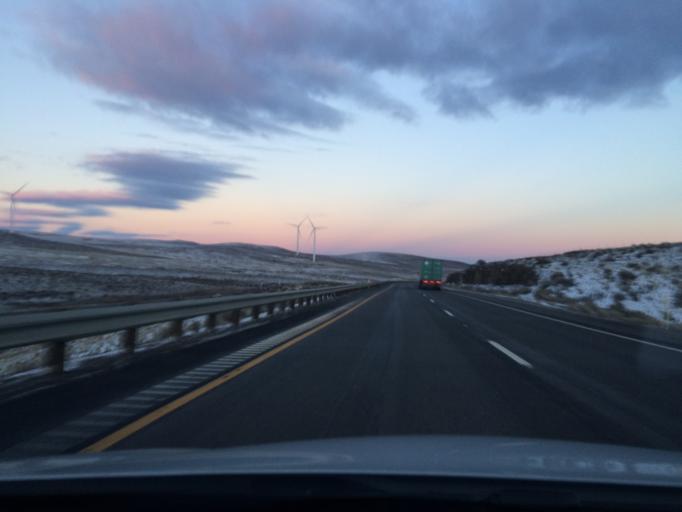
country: US
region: Washington
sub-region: Grant County
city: Mattawa
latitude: 46.9424
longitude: -120.1136
